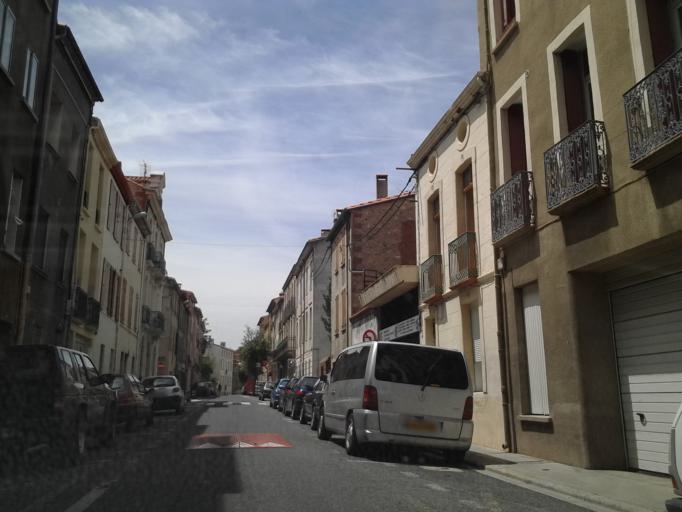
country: FR
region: Languedoc-Roussillon
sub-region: Departement des Pyrenees-Orientales
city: Prades
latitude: 42.6173
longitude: 2.4268
